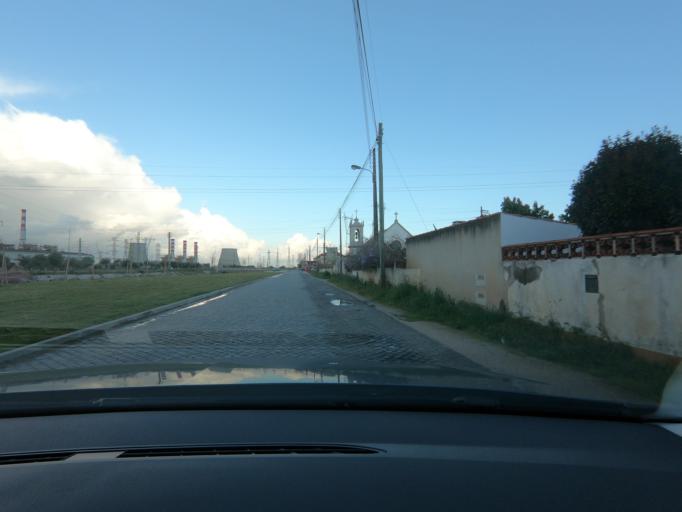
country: PT
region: Lisbon
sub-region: Alenquer
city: Carregado
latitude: 39.0120
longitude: -8.9636
